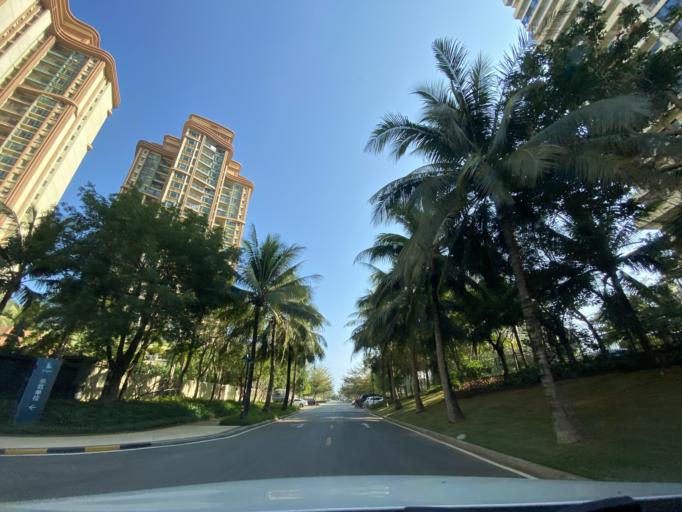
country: CN
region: Hainan
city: Yingzhou
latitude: 18.4168
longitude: 109.8967
